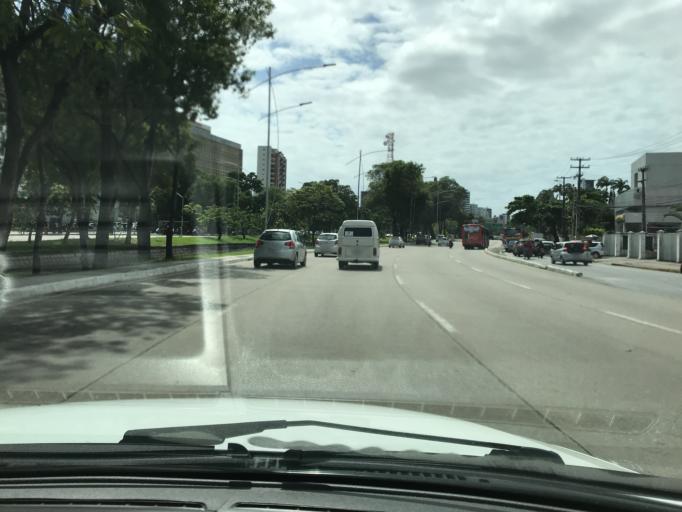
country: BR
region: Pernambuco
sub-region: Recife
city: Recife
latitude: -8.0558
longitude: -34.8978
